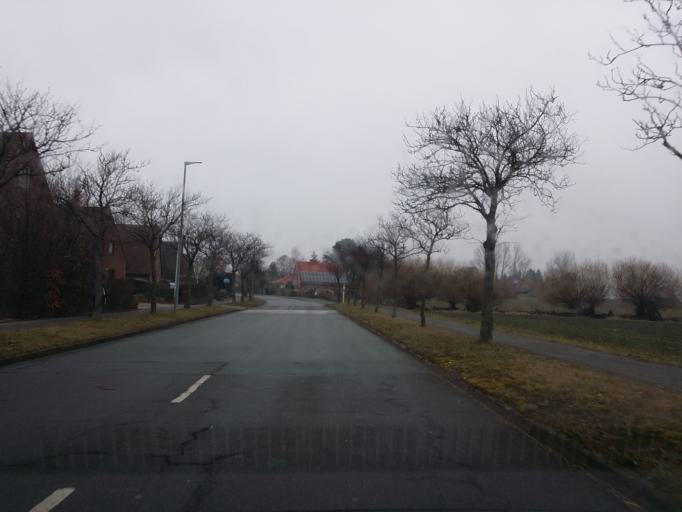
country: DE
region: Schleswig-Holstein
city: Burg auf Fehmarn
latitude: 54.4198
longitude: 11.2100
